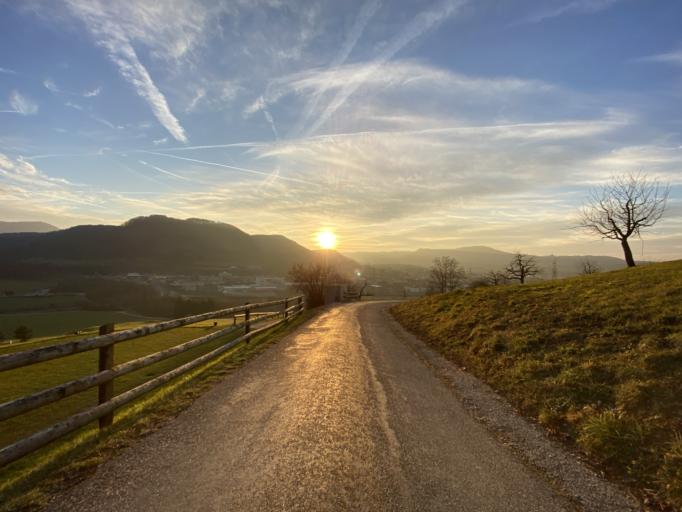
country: CH
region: Aargau
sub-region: Bezirk Laufenburg
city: Frick
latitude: 47.5064
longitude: 8.0399
